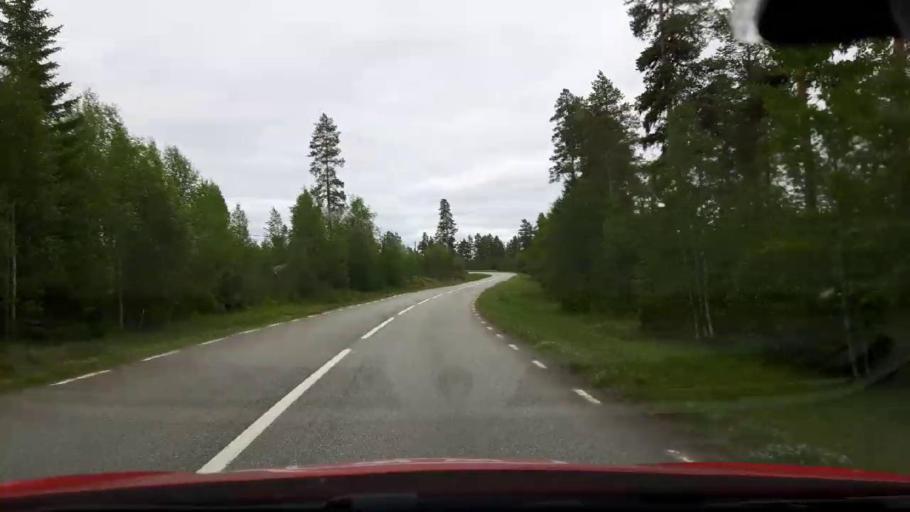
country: SE
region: Jaemtland
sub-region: Stroemsunds Kommun
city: Stroemsund
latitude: 63.3761
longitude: 15.6930
